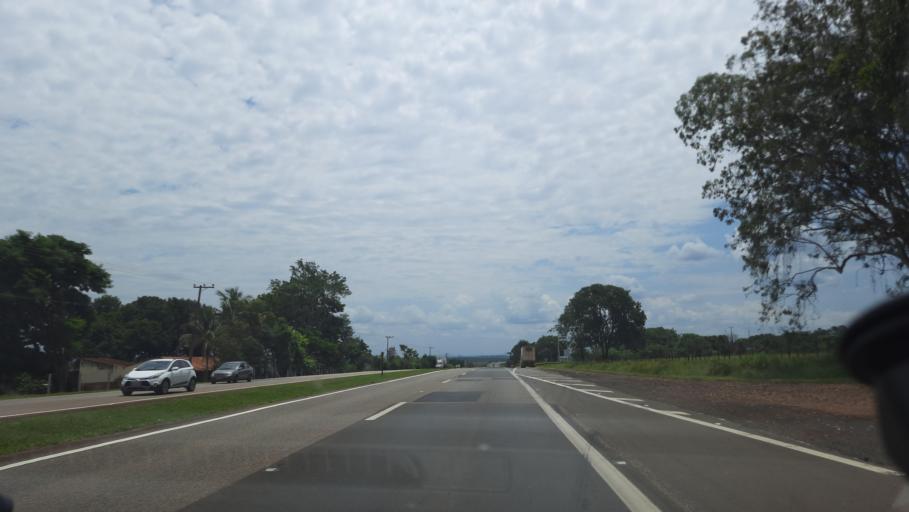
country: BR
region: Sao Paulo
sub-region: Casa Branca
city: Casa Branca
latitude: -21.7228
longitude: -47.0791
